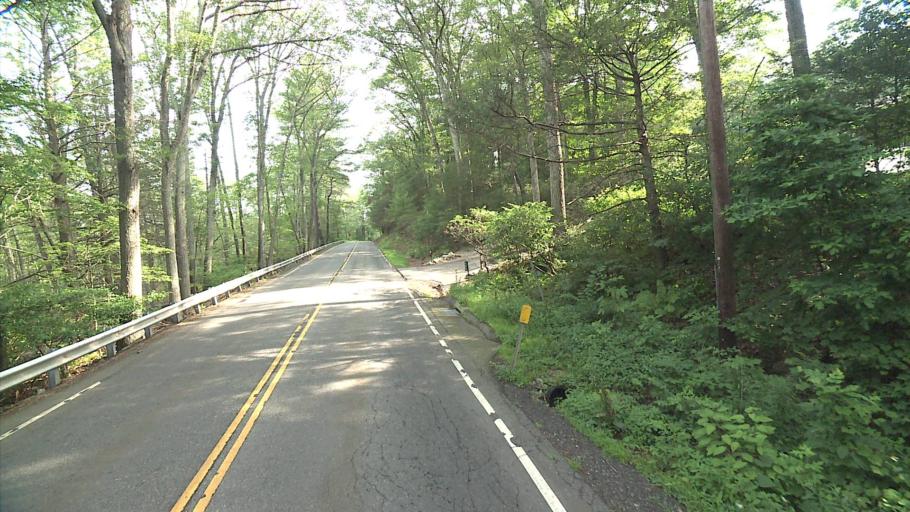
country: US
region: Connecticut
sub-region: Windham County
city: Quinebaug
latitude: 41.9903
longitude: -72.0165
